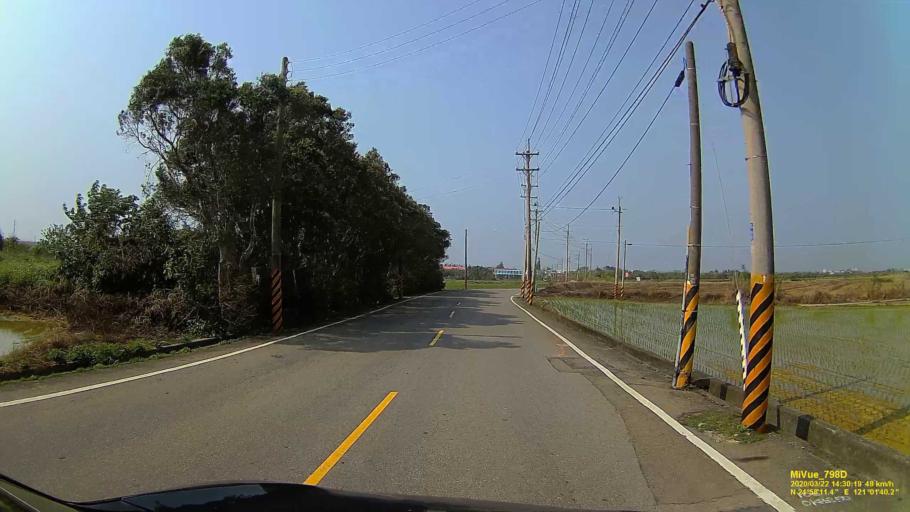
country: TW
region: Taiwan
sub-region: Hsinchu
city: Zhubei
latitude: 24.9703
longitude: 121.0279
